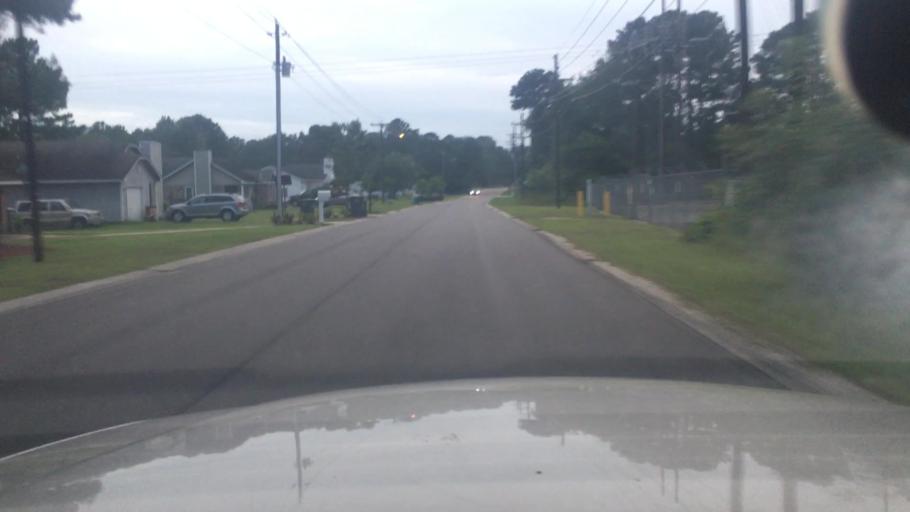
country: US
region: North Carolina
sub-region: Cumberland County
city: Hope Mills
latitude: 34.9627
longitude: -78.9400
